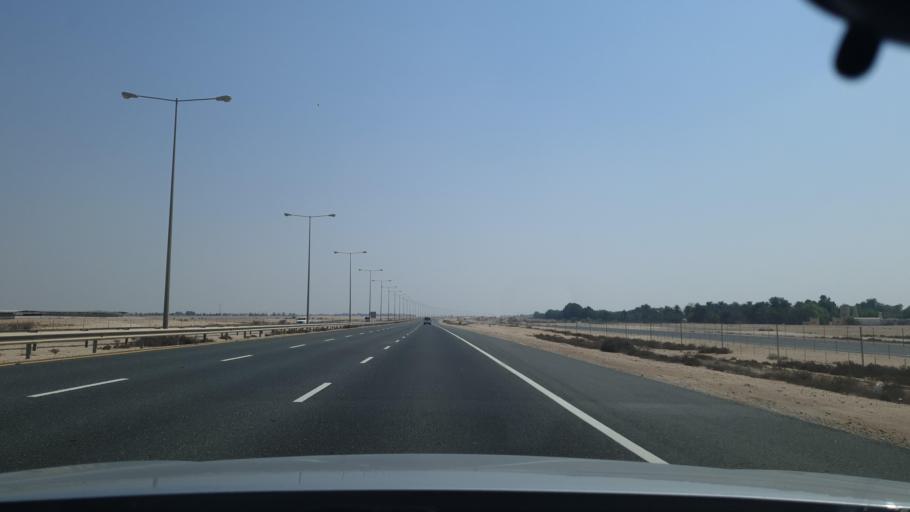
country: QA
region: Al Khawr
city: Al Khawr
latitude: 25.7824
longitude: 51.4006
